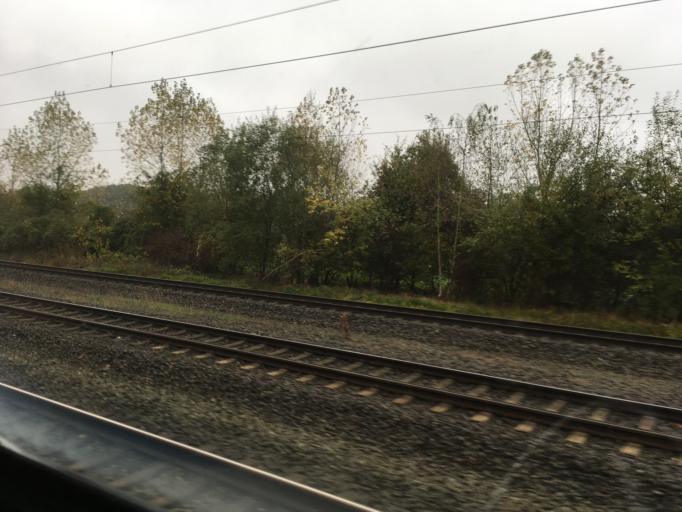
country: DE
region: North Rhine-Westphalia
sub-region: Regierungsbezirk Munster
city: Muenster
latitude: 51.9908
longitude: 7.6791
